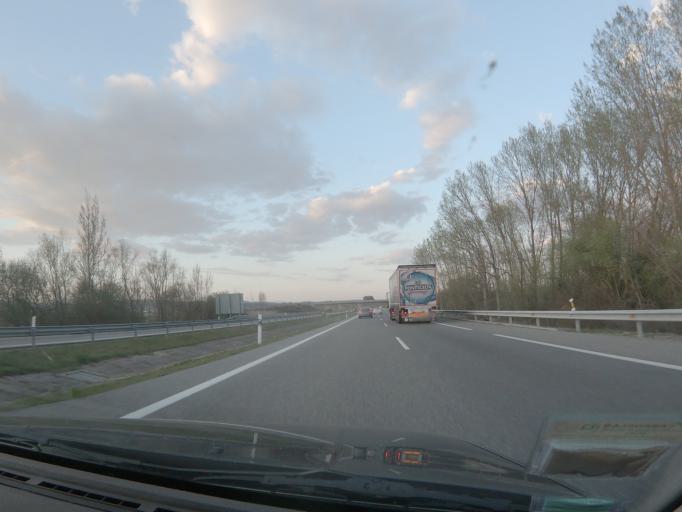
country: ES
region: Castille and Leon
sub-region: Provincia de Leon
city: Carracedelo
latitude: 42.5728
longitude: -6.7136
